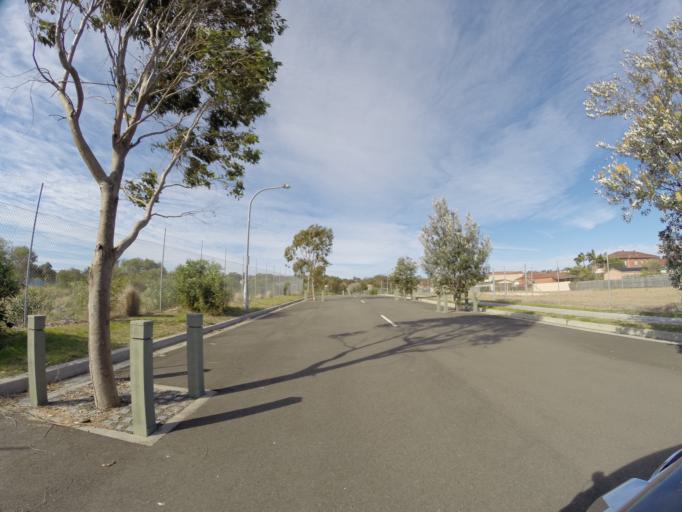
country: AU
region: New South Wales
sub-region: Randwick
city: South Coogee
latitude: -33.9334
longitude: 151.2453
